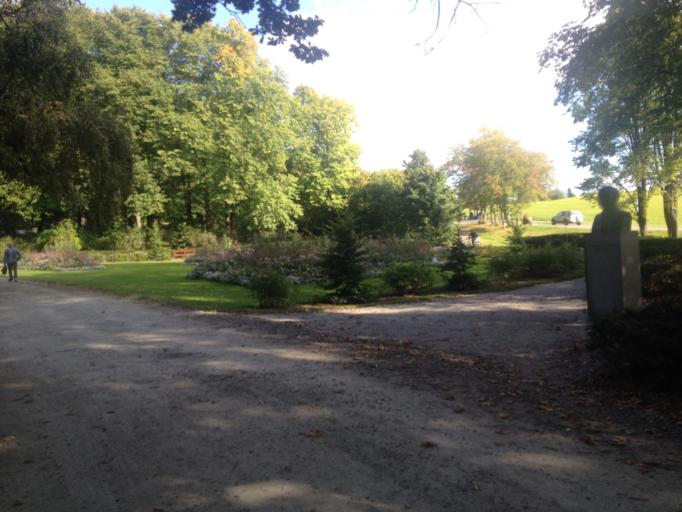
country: NO
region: Akershus
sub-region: As
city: As
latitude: 59.6649
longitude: 10.7668
